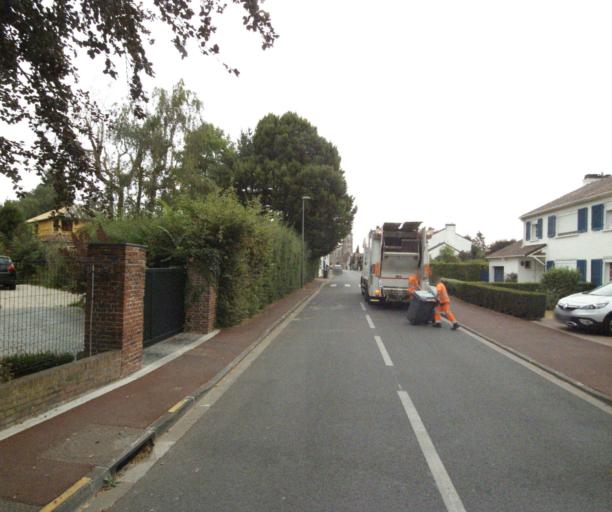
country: FR
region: Nord-Pas-de-Calais
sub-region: Departement du Nord
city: Bondues
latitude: 50.7014
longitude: 3.0903
